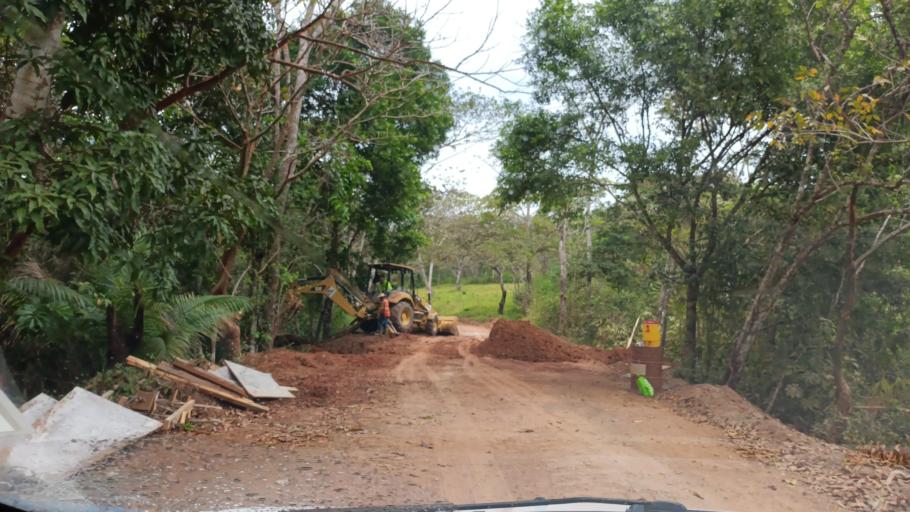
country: PA
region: Panama
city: La Cabima
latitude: 9.1285
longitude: -79.5048
